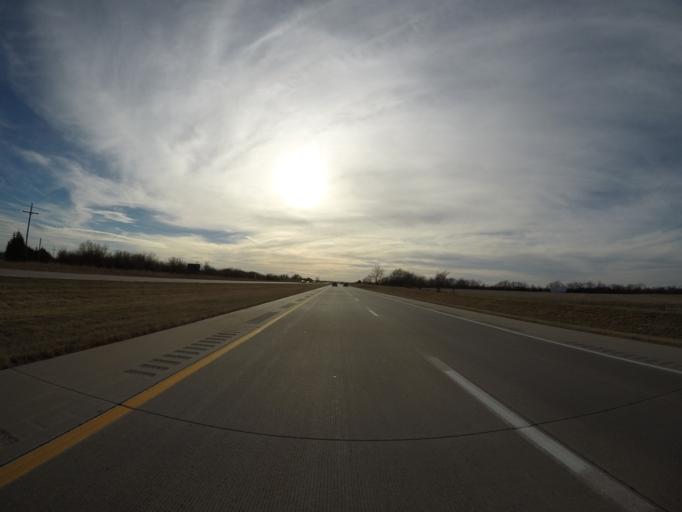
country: US
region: Kansas
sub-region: Johnson County
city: Edgerton
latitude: 38.7305
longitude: -95.0288
